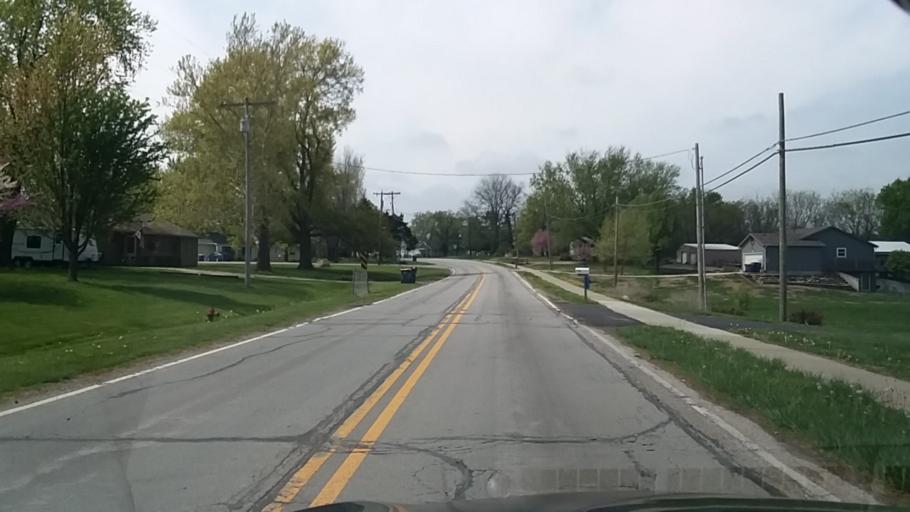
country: US
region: Kansas
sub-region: Johnson County
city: De Soto
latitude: 38.9730
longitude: -94.9817
